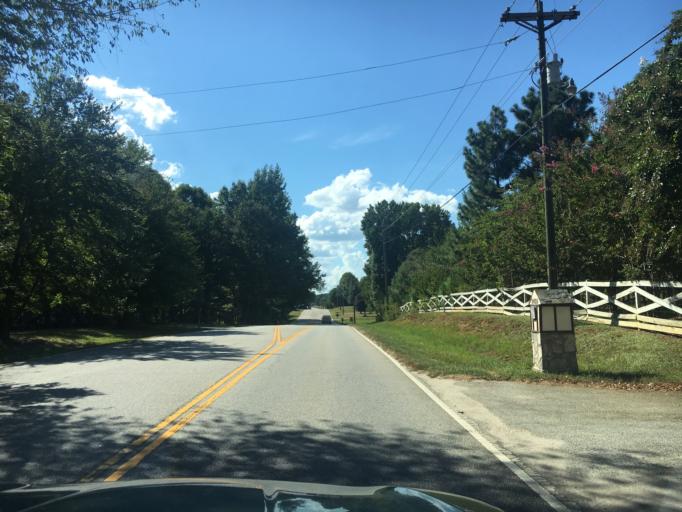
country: US
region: South Carolina
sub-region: Greenville County
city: Five Forks
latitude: 34.8237
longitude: -82.2327
